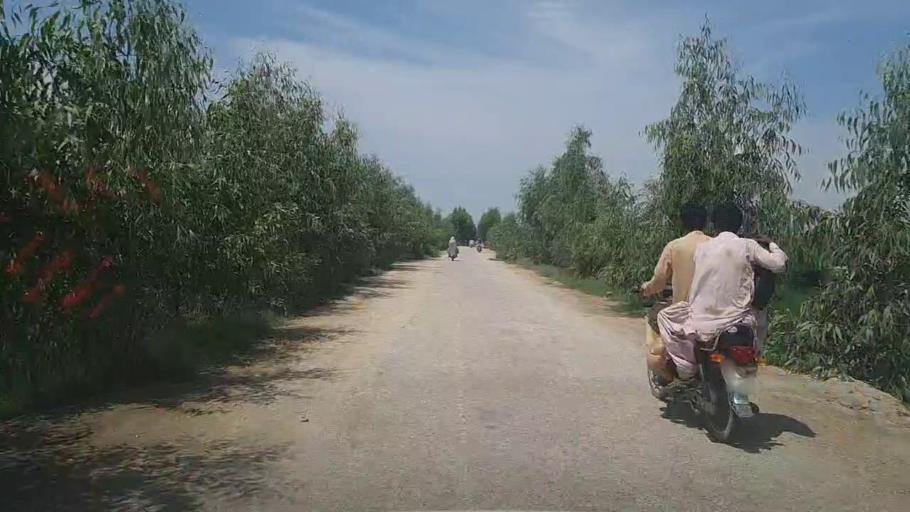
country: PK
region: Sindh
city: Kandhkot
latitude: 28.2942
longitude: 69.2373
